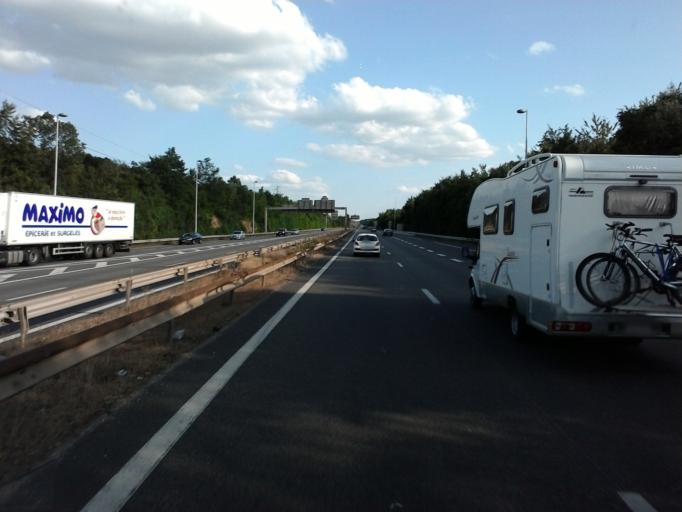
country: FR
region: Lorraine
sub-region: Departement de Meurthe-et-Moselle
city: Laxou
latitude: 48.6900
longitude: 6.1162
